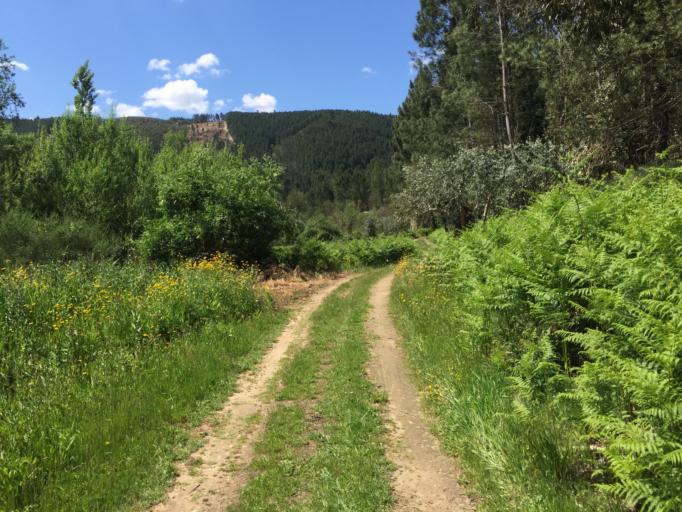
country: PT
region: Coimbra
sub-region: Pampilhosa da Serra
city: Pampilhosa da Serra
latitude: 40.0709
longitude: -7.7763
